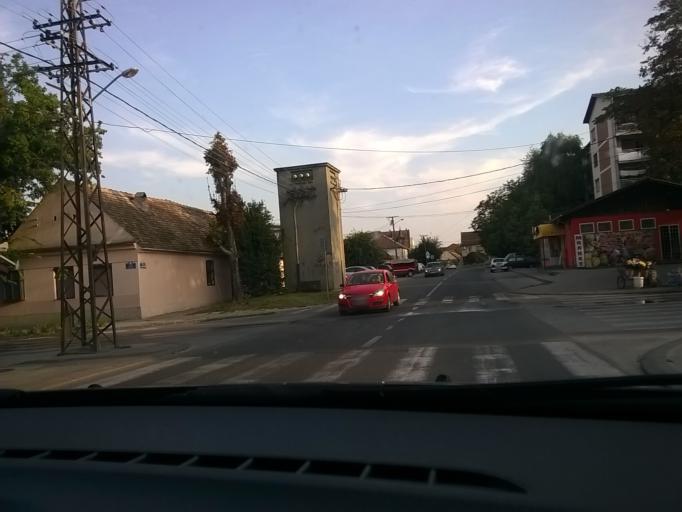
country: RS
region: Autonomna Pokrajina Vojvodina
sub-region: Juznobanatski Okrug
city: Vrsac
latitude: 45.1169
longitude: 21.2851
